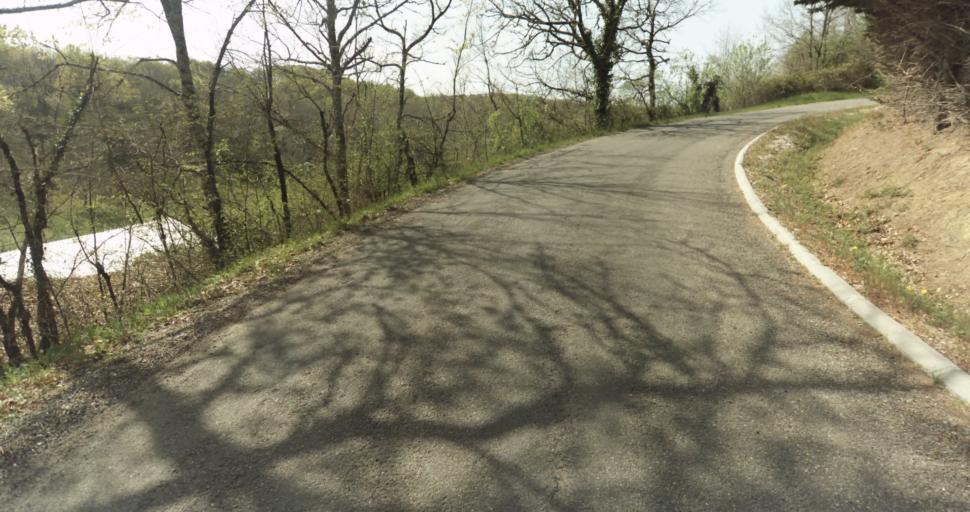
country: FR
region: Midi-Pyrenees
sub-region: Departement du Tarn-et-Garonne
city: Moissac
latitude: 44.1267
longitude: 1.0906
